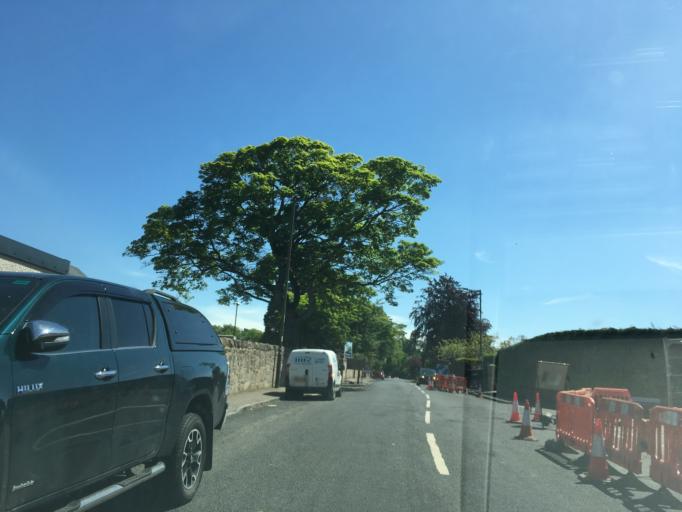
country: GB
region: Scotland
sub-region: Fife
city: Aberdour
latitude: 55.9747
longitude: -3.2980
